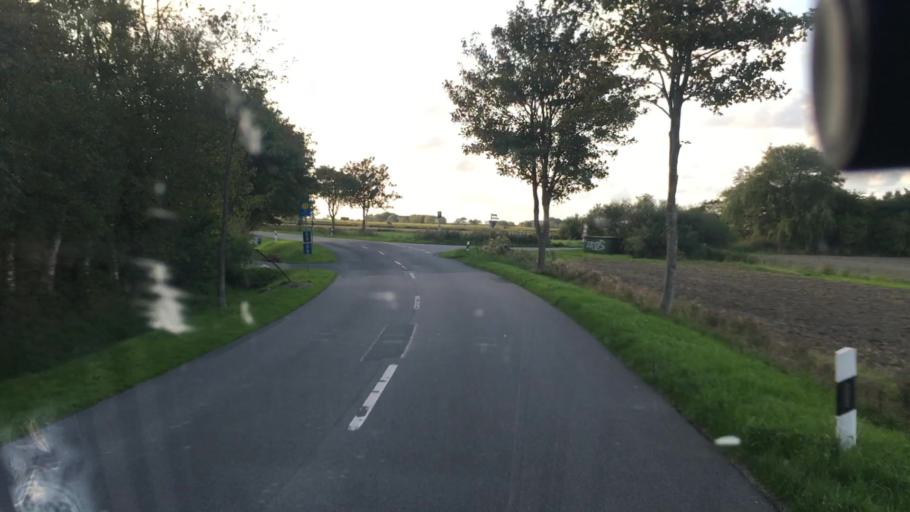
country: DE
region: Lower Saxony
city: Neuharlingersiel
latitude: 53.6854
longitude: 7.7013
